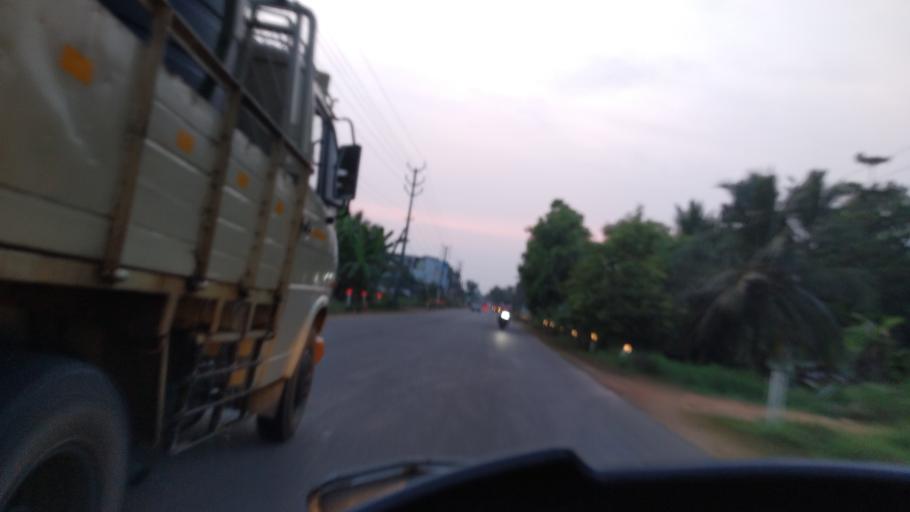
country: IN
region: Kerala
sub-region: Kottayam
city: Kottayam
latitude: 9.5923
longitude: 76.4476
